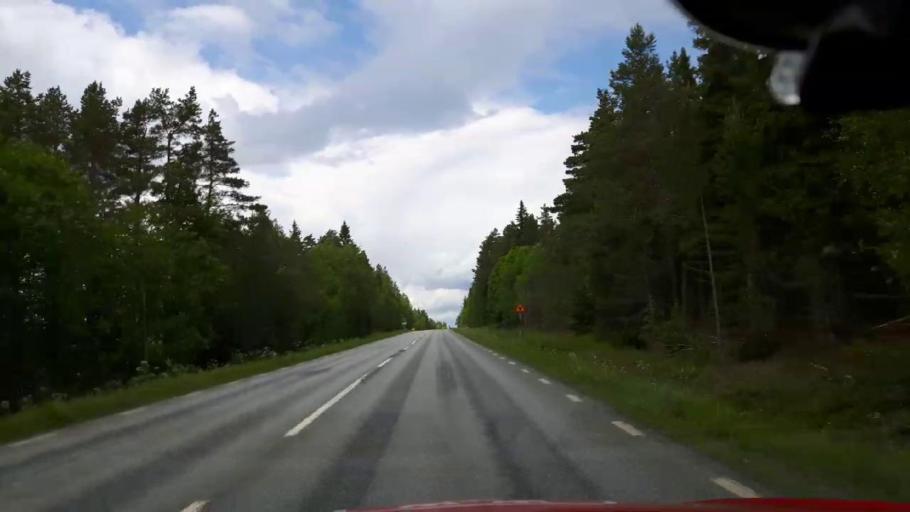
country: SE
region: Jaemtland
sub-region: Krokoms Kommun
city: Krokom
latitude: 63.3666
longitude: 14.3926
